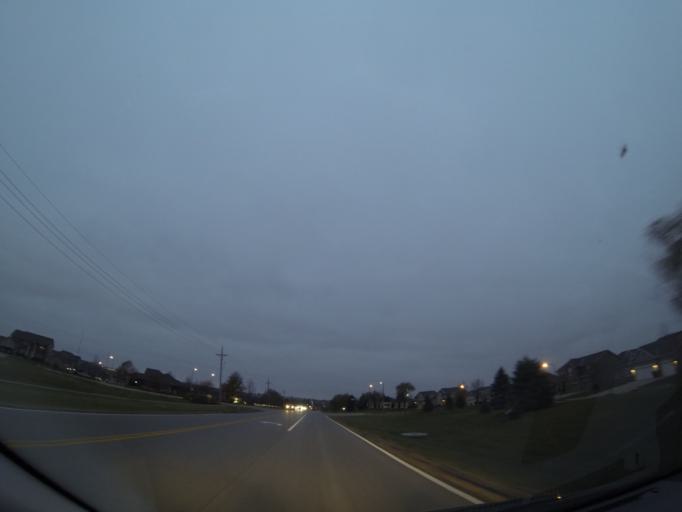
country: US
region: Nebraska
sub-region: Douglas County
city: Elkhorn
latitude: 41.2776
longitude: -96.1810
